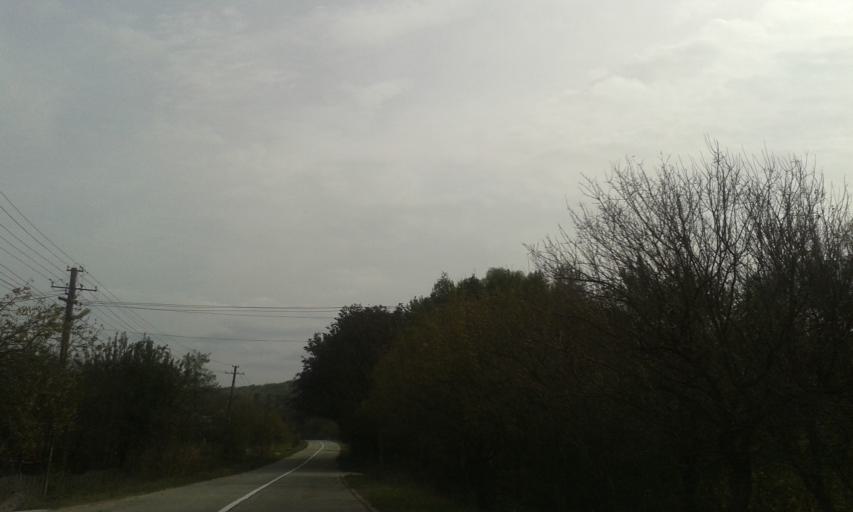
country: RO
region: Valcea
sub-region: Comuna Gradistea
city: Gradistea
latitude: 44.9075
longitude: 23.7932
